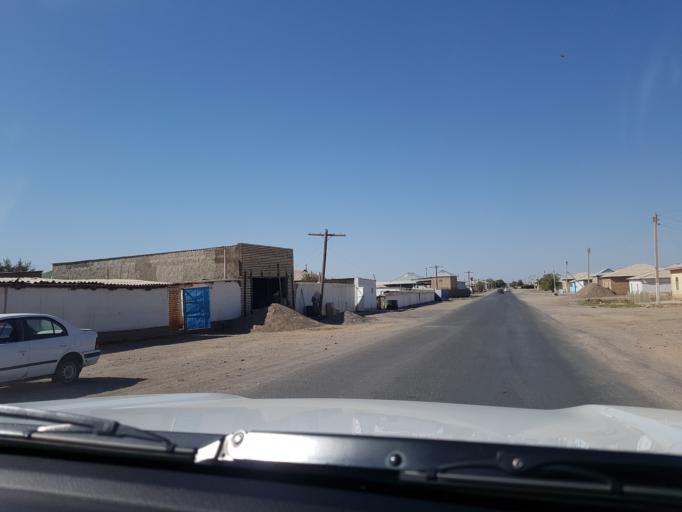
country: IR
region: Razavi Khorasan
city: Sarakhs
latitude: 36.5145
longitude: 61.2221
